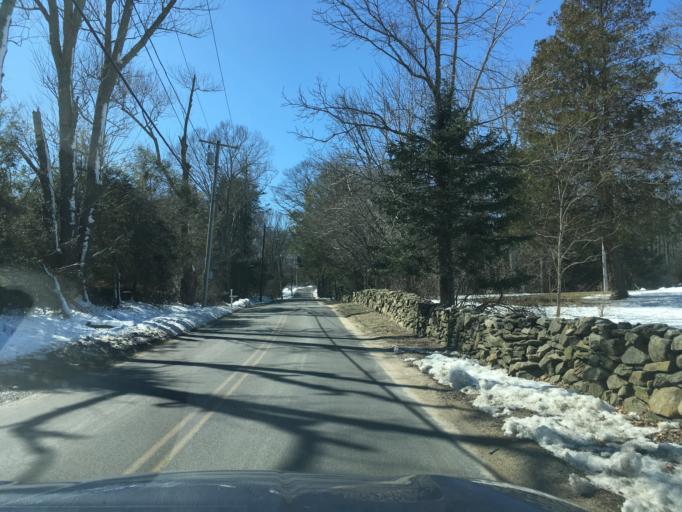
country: US
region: Rhode Island
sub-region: Washington County
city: Exeter
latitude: 41.6086
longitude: -71.5067
